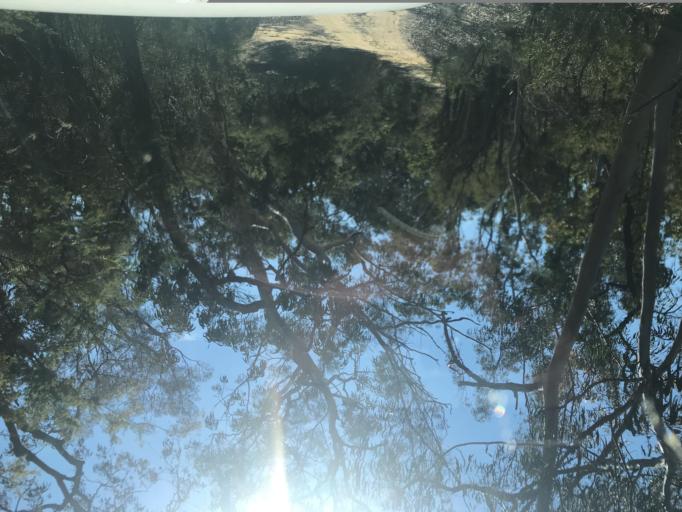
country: AU
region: New South Wales
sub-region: Wyong Shire
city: Little Jilliby
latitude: -33.1503
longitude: 151.1005
